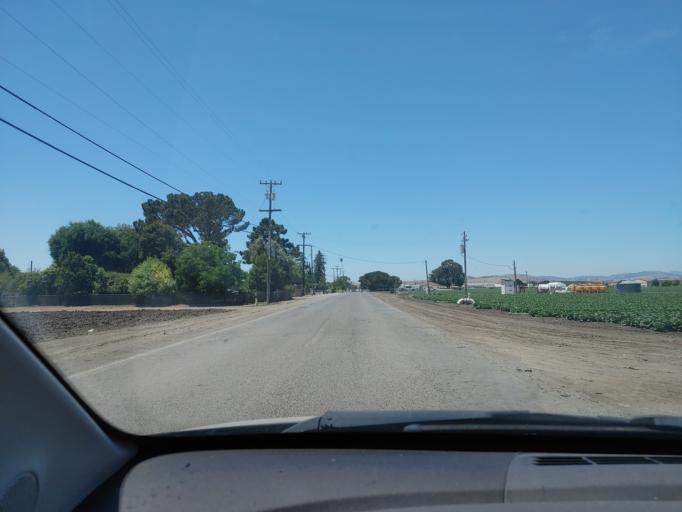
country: US
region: California
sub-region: San Benito County
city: Hollister
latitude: 36.8690
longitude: -121.3922
